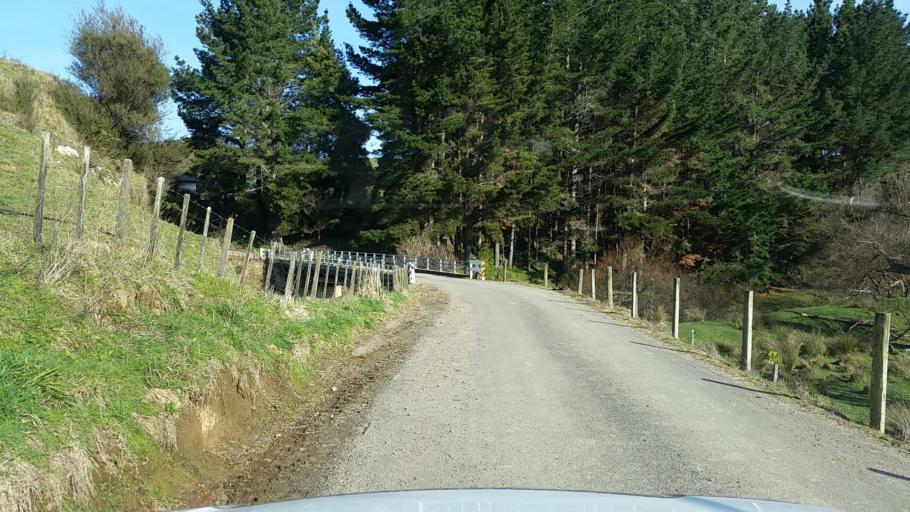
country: NZ
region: Taranaki
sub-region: South Taranaki District
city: Eltham
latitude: -39.3193
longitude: 174.5303
